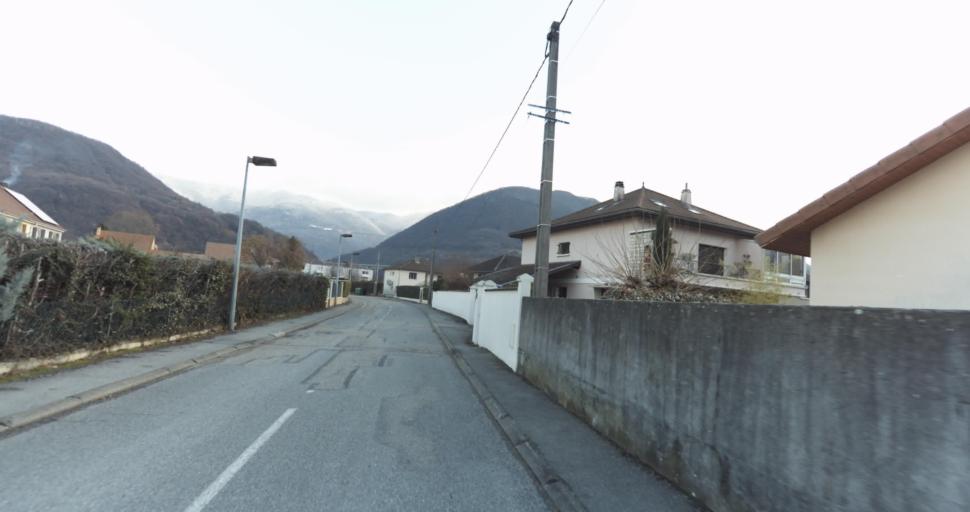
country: FR
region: Rhone-Alpes
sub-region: Departement de l'Isere
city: Vif
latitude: 45.0555
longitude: 5.6769
